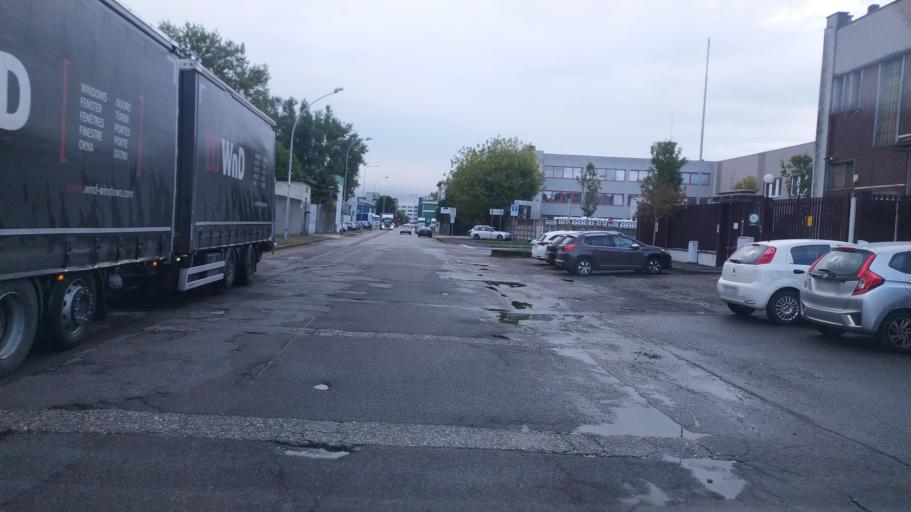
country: IT
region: Lombardy
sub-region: Citta metropolitana di Milano
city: Trezzano sul Naviglio
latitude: 45.4309
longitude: 9.0686
